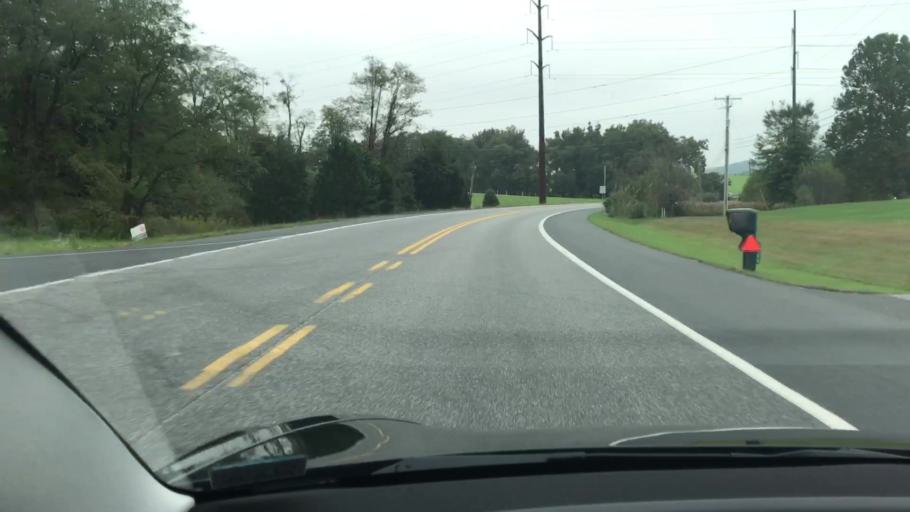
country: US
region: Pennsylvania
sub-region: Cumberland County
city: Lower Allen
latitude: 40.1554
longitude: -76.8839
